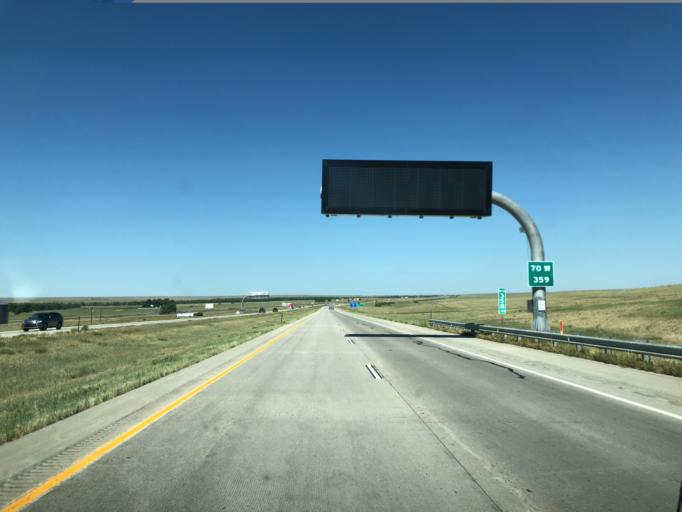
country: US
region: Colorado
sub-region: Lincoln County
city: Limon
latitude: 39.2734
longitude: -103.7233
